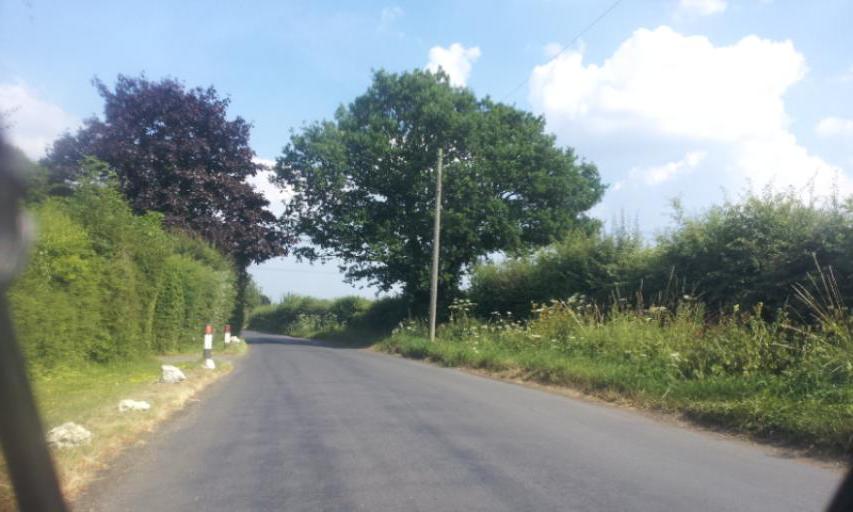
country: GB
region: England
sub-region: Kent
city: Yalding
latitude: 51.2028
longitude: 0.4267
